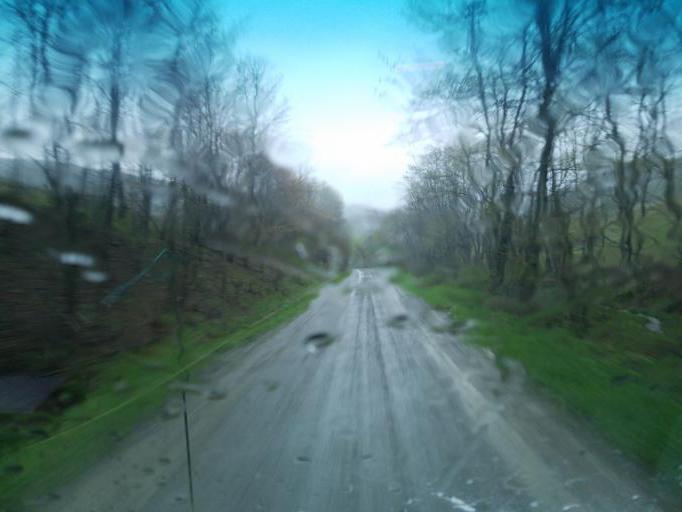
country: US
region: Pennsylvania
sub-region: Tioga County
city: Westfield
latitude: 41.9020
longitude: -77.7184
